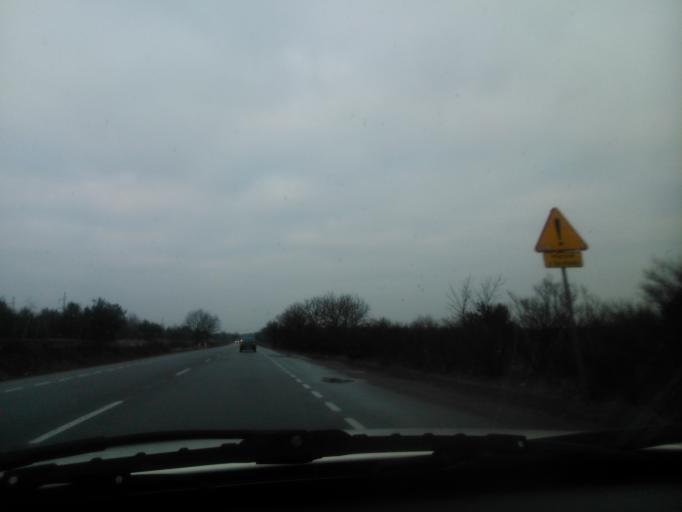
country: PL
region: Kujawsko-Pomorskie
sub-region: Torun
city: Torun
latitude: 53.0458
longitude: 18.6163
